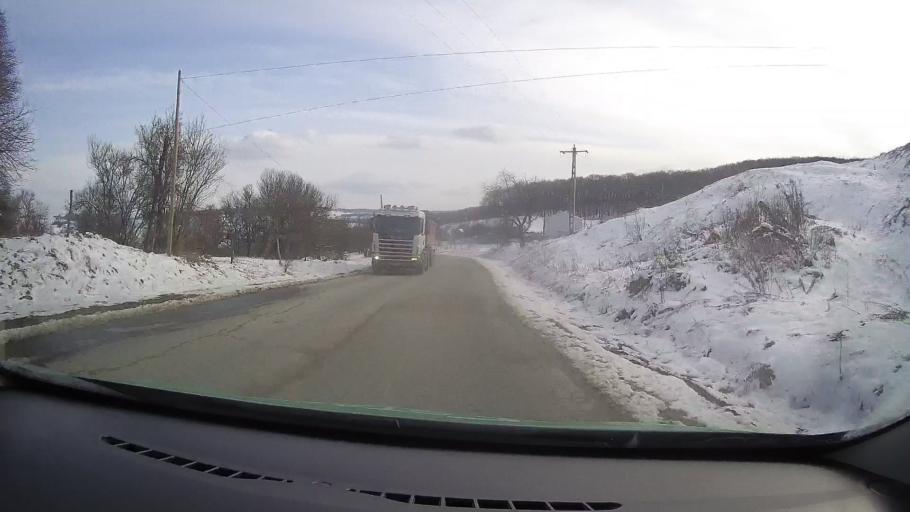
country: RO
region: Sibiu
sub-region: Oras Agnita
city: Ruja
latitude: 45.9855
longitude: 24.6859
